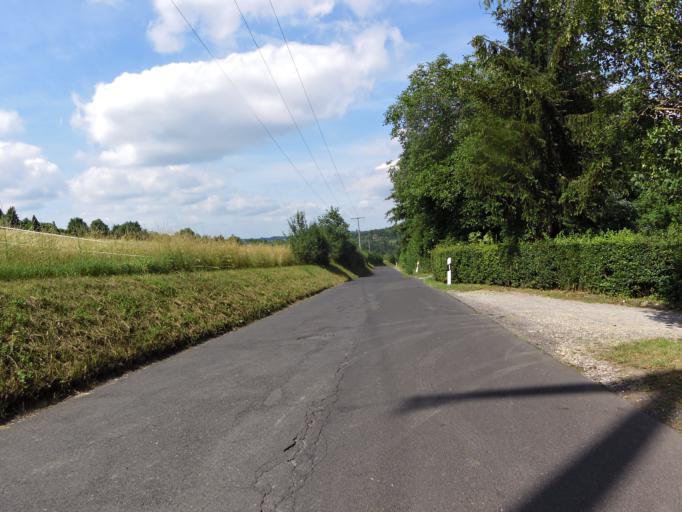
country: DE
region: Bavaria
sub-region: Regierungsbezirk Unterfranken
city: Wuerzburg
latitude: 49.8147
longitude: 9.9291
